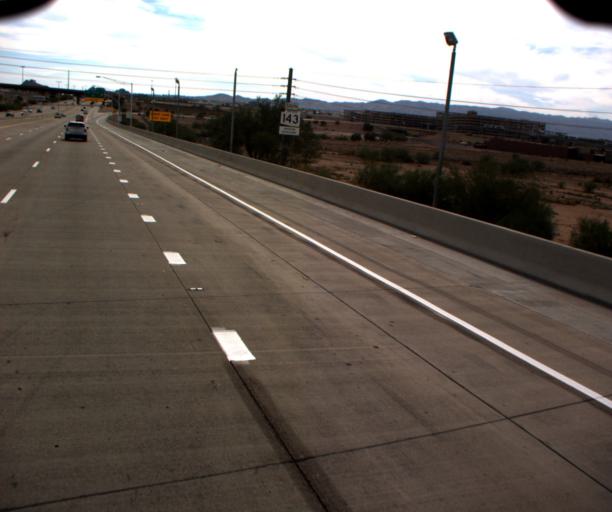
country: US
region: Arizona
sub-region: Maricopa County
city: Tempe Junction
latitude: 33.4422
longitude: -111.9804
